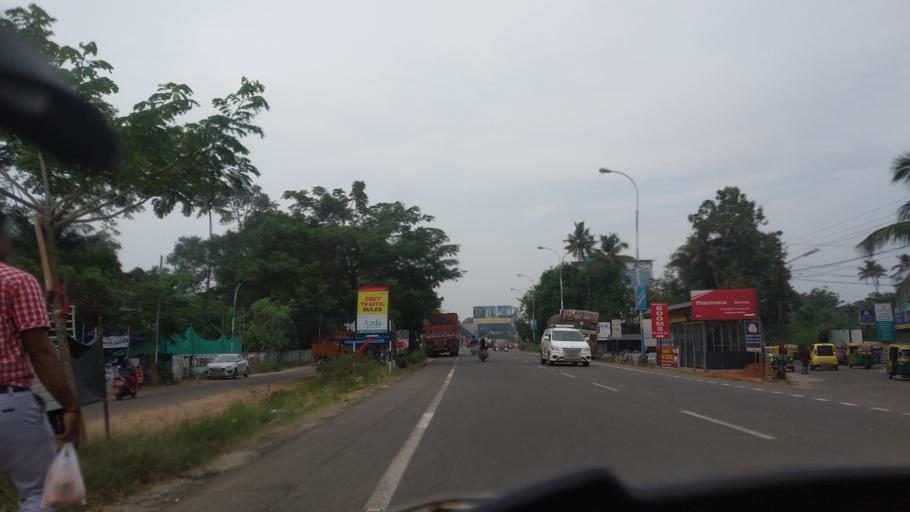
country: IN
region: Kerala
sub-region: Ernakulam
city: Elur
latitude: 10.0481
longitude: 76.2956
